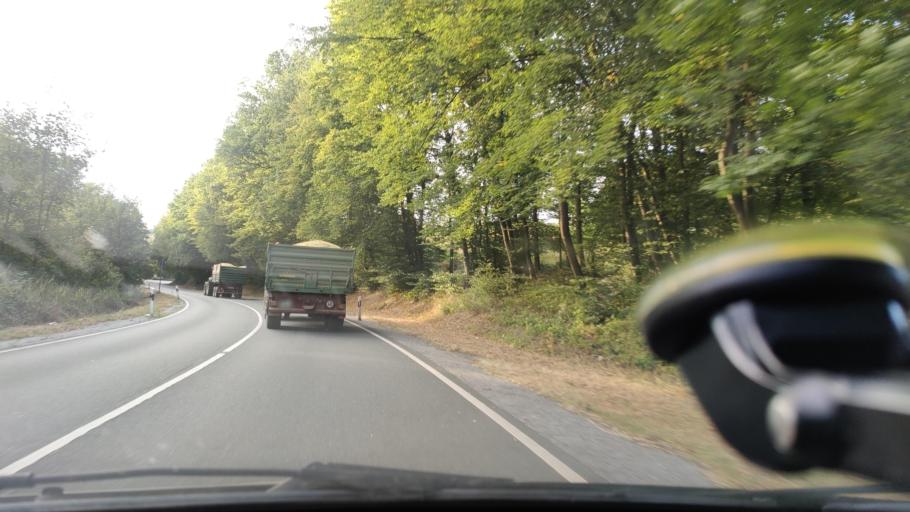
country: DE
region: North Rhine-Westphalia
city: Schwerte
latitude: 51.3913
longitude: 7.5847
